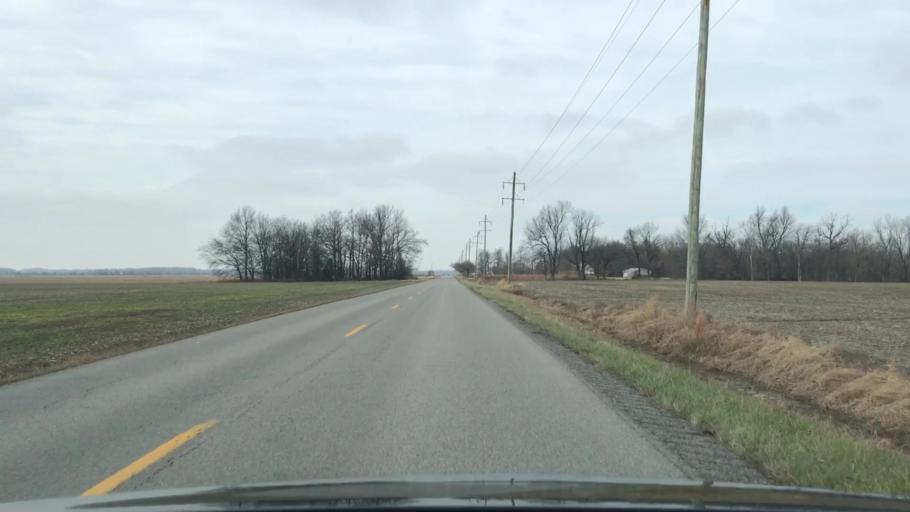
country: US
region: Kentucky
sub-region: McLean County
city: Calhoun
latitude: 37.5265
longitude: -87.2960
